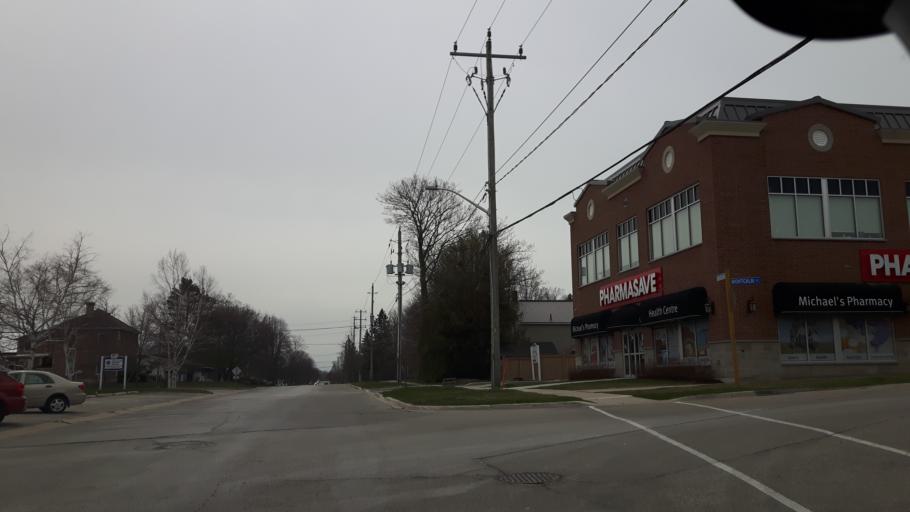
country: CA
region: Ontario
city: Goderich
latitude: 43.7496
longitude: -81.7046
